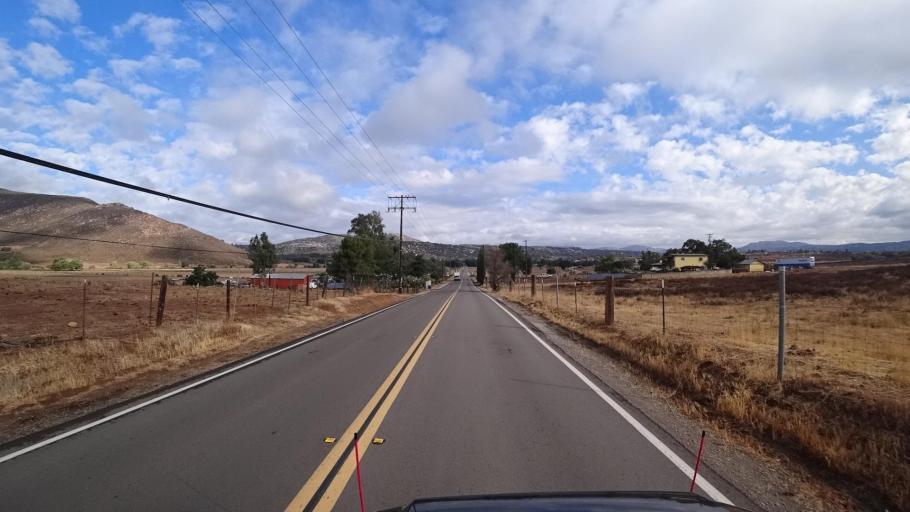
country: MX
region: Baja California
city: Tecate
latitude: 32.6131
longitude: -116.6133
